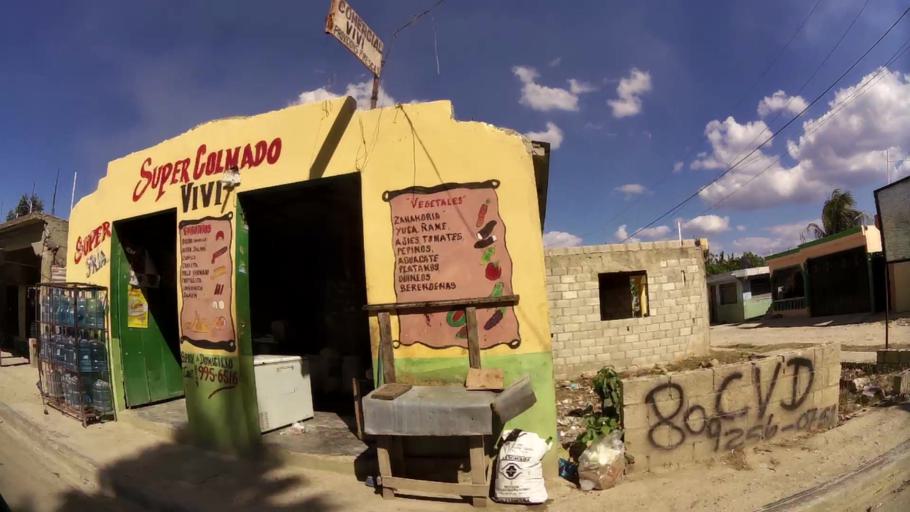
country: DO
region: Santo Domingo
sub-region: Santo Domingo
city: Santo Domingo Este
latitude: 18.4669
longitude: -69.7674
